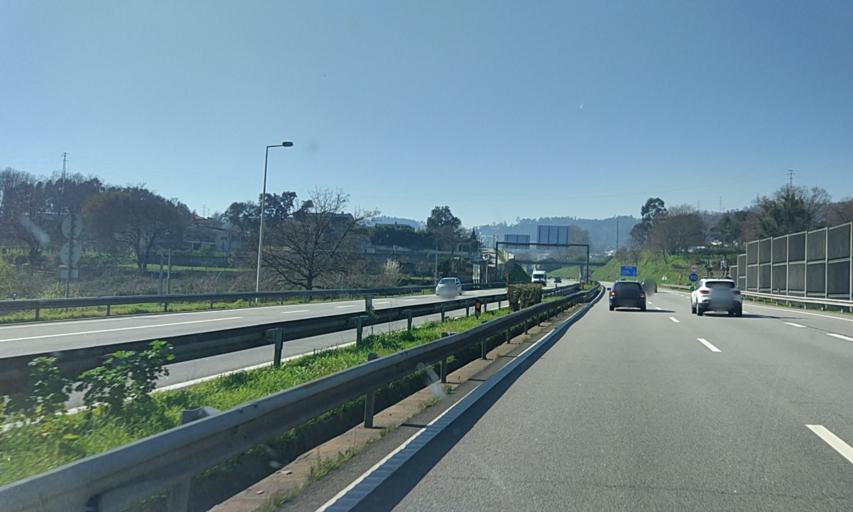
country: PT
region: Porto
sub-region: Paredes
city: Casteloes de Cepeda
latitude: 41.1983
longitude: -8.3413
